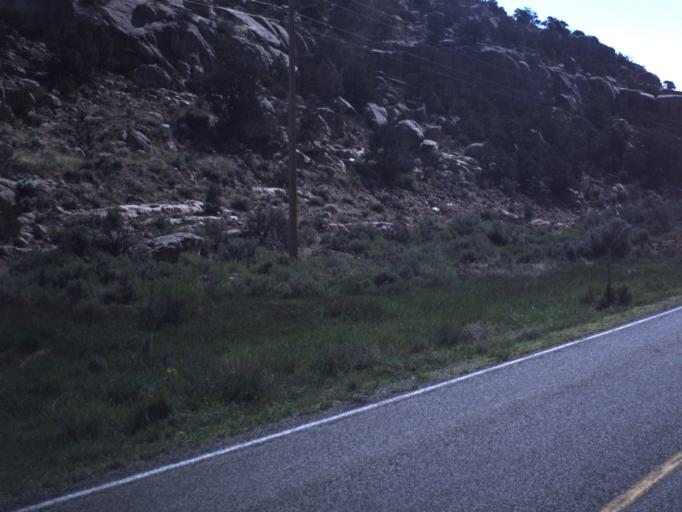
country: US
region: Utah
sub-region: Duchesne County
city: Duchesne
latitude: 40.3083
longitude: -110.6358
